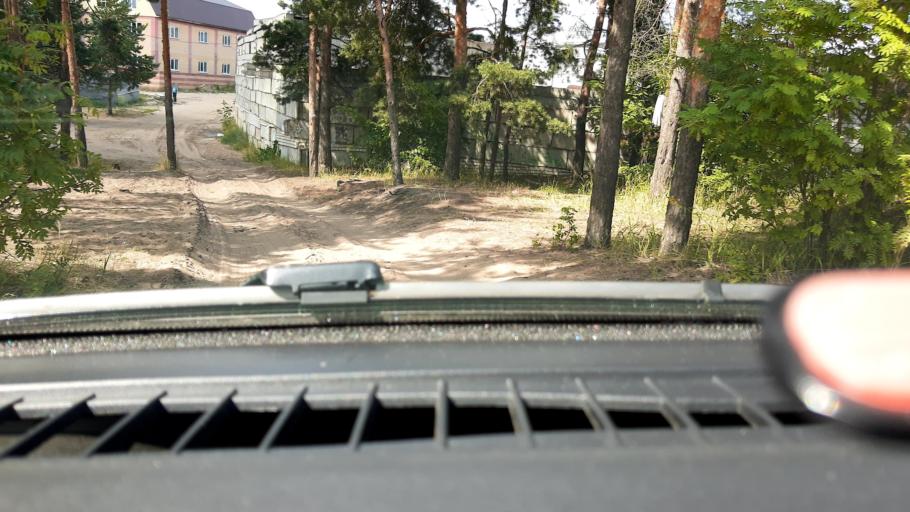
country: RU
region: Nizjnij Novgorod
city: Gorbatovka
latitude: 56.3800
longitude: 43.7658
